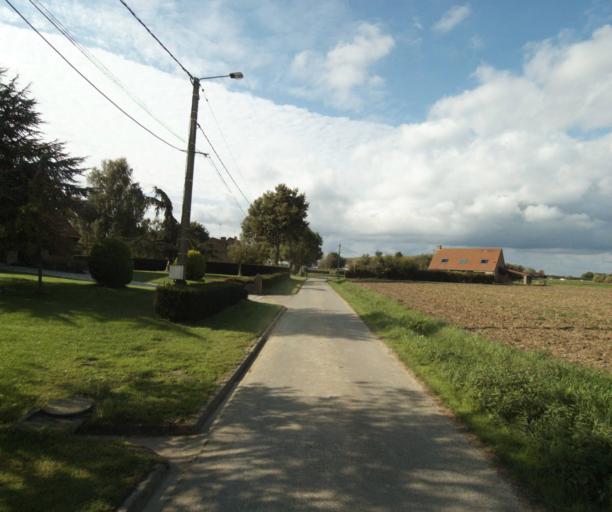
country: FR
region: Nord-Pas-de-Calais
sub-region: Departement du Nord
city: Ennetieres-en-Weppes
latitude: 50.6458
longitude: 2.9206
